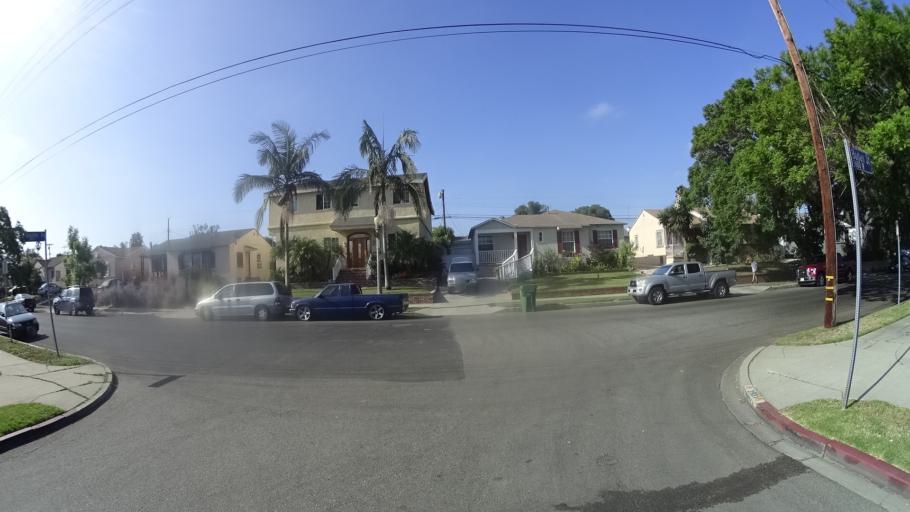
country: US
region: California
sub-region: Los Angeles County
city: Culver City
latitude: 34.0282
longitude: -118.3702
